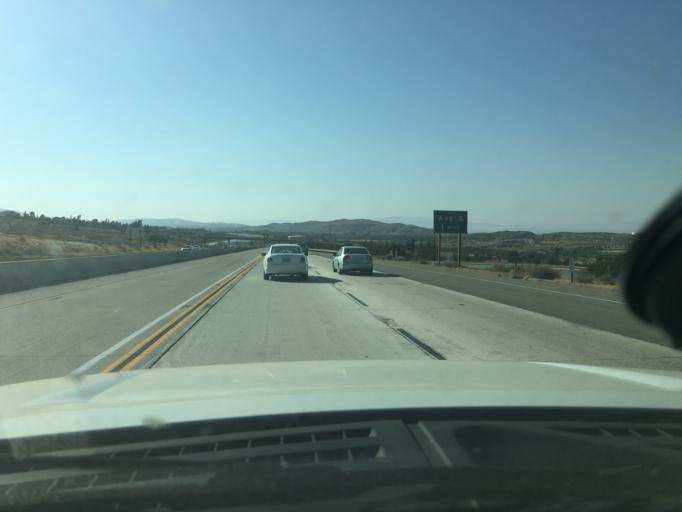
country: US
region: California
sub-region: Los Angeles County
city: Palmdale
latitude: 34.5421
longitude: -118.1247
